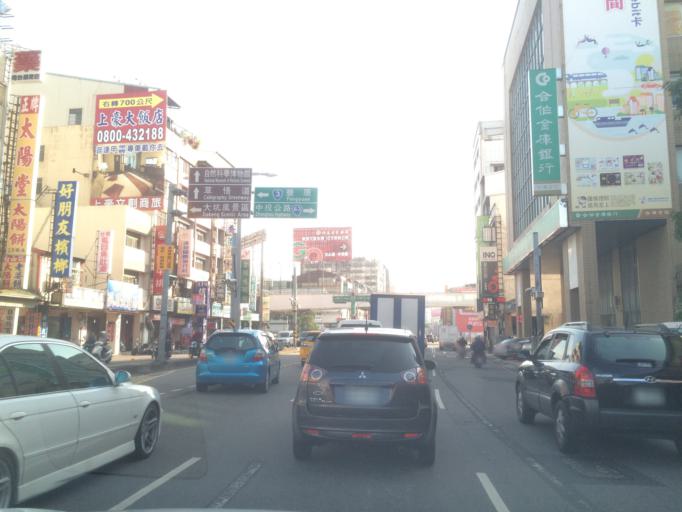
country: TW
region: Taiwan
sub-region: Taichung City
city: Taichung
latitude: 24.1748
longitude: 120.6710
